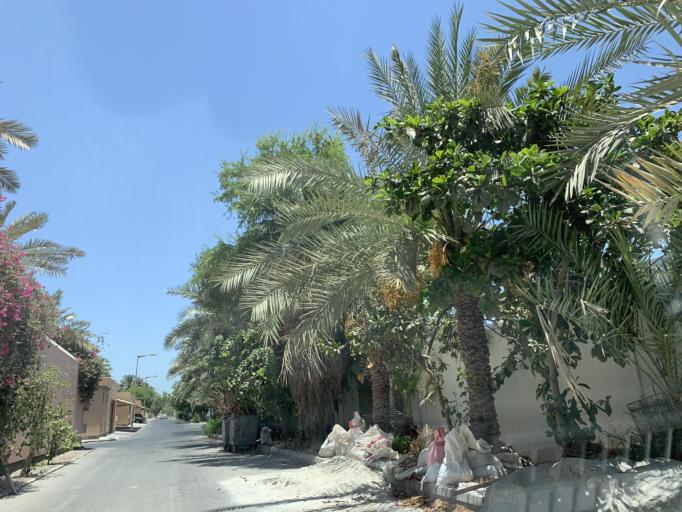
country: BH
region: Manama
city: Jidd Hafs
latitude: 26.2225
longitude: 50.4870
